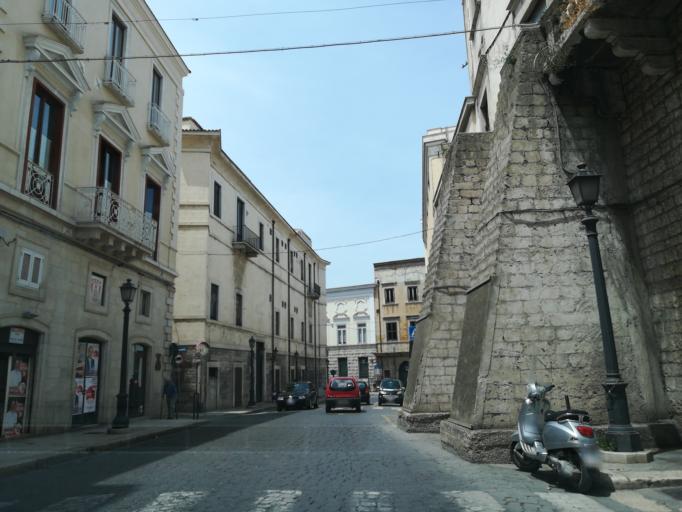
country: IT
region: Apulia
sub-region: Provincia di Barletta - Andria - Trani
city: Barletta
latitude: 41.3196
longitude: 16.2841
